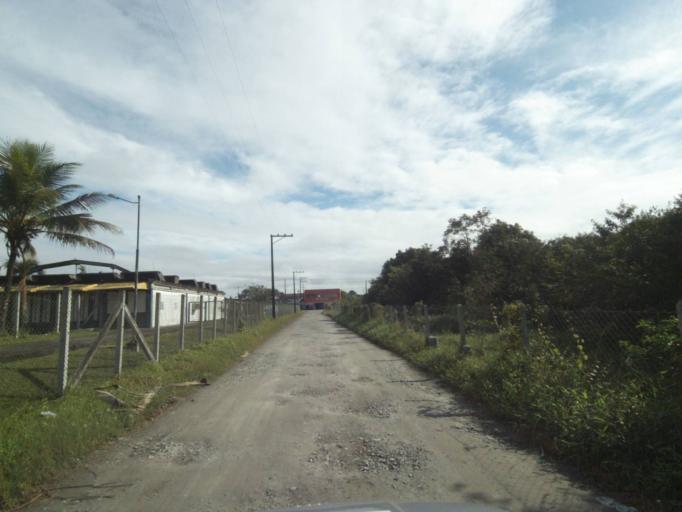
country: BR
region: Parana
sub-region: Paranagua
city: Paranagua
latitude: -25.5629
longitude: -48.5627
